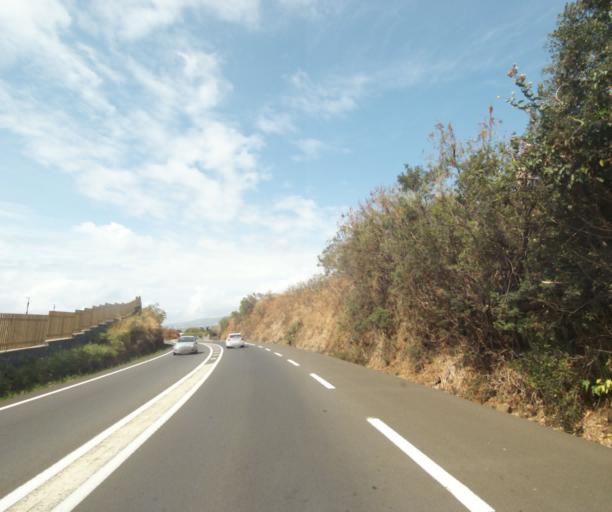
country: RE
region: Reunion
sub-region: Reunion
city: Saint-Paul
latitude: -21.0296
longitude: 55.2733
